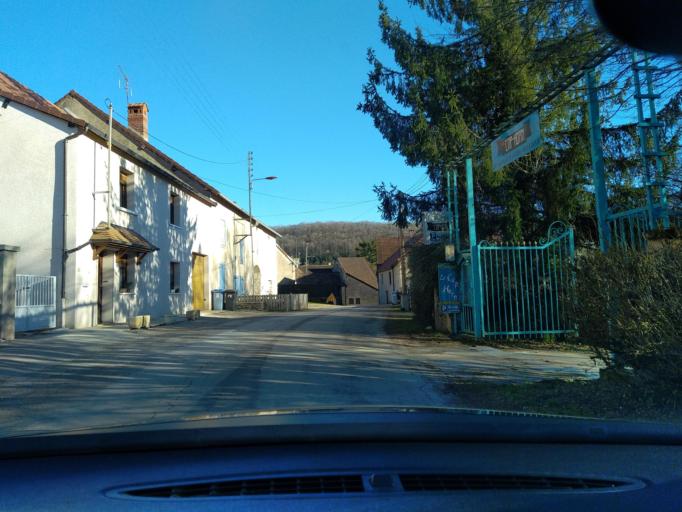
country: FR
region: Franche-Comte
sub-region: Departement du Jura
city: Clairvaux-les-Lacs
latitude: 46.6978
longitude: 5.7265
